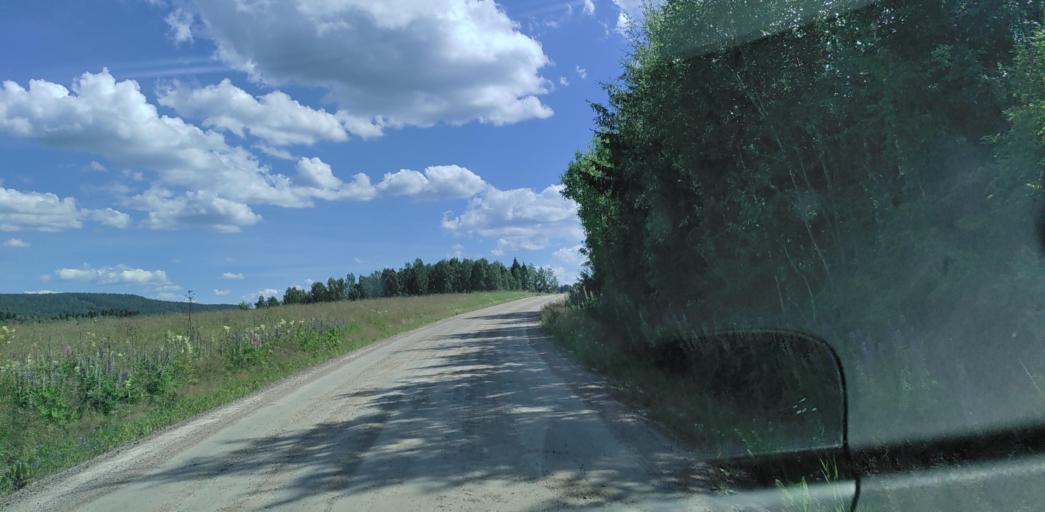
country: SE
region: Vaermland
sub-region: Hagfors Kommun
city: Ekshaerad
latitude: 60.1242
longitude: 13.4804
